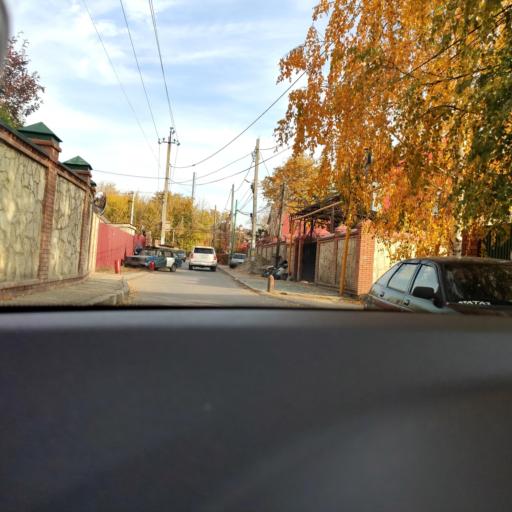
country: RU
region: Samara
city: Samara
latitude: 53.2663
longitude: 50.1920
